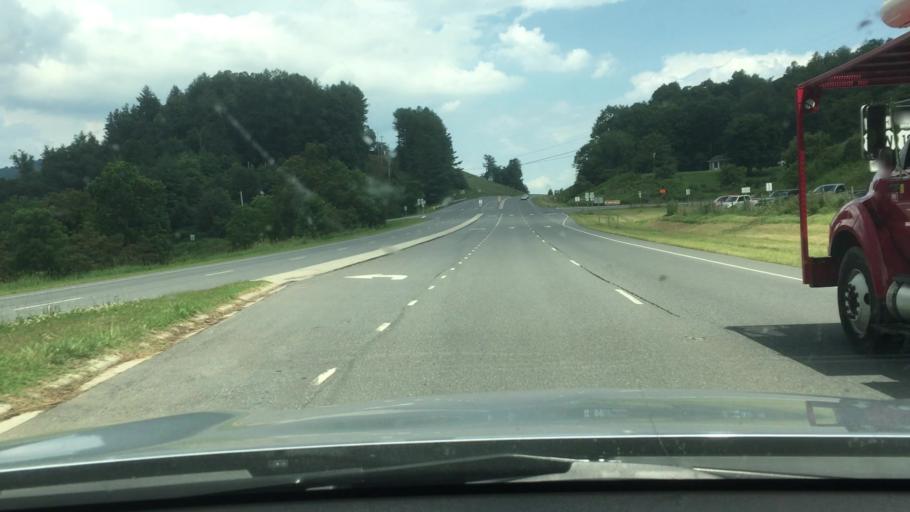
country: US
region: North Carolina
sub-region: Yancey County
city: Burnsville
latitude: 35.9133
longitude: -82.3994
